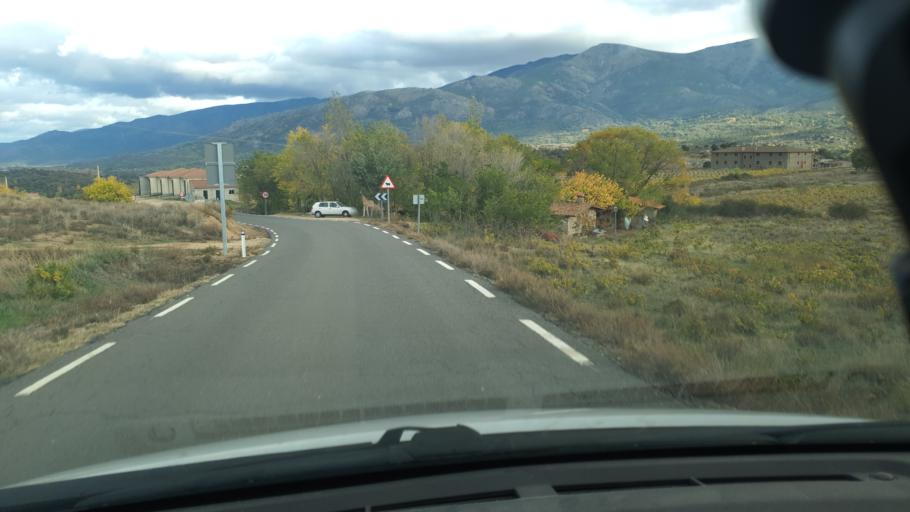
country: ES
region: Castille and Leon
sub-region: Provincia de Avila
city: Burgohondo
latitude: 40.4090
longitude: -4.7905
